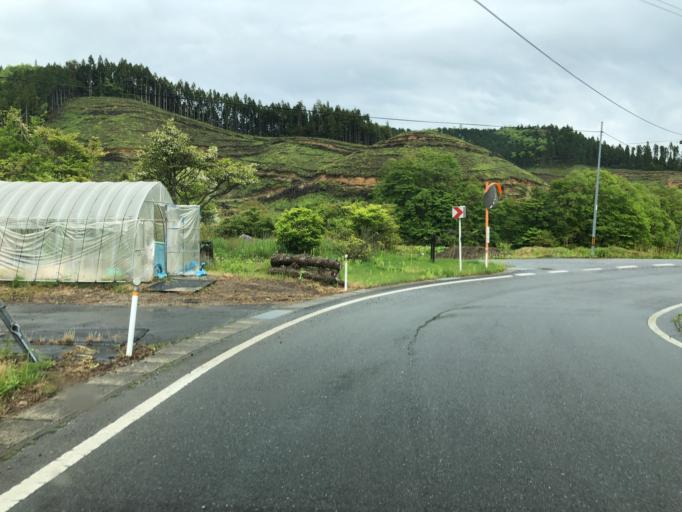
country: JP
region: Fukushima
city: Ishikawa
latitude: 36.9989
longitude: 140.6108
